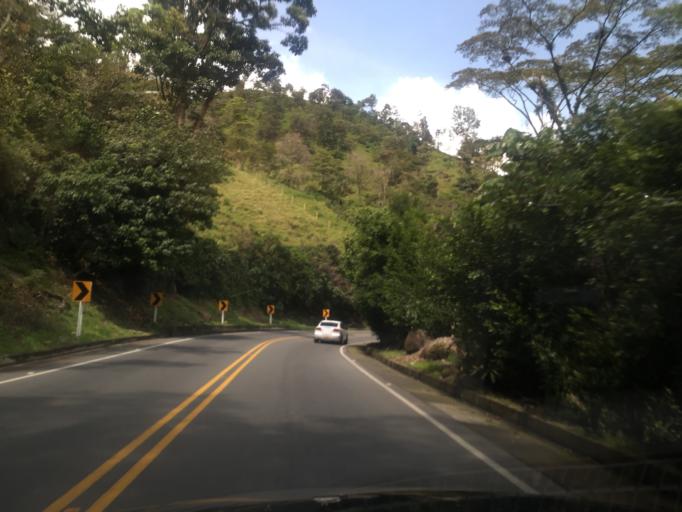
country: CO
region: Caldas
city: Chinchina
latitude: 4.9881
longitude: -75.5815
